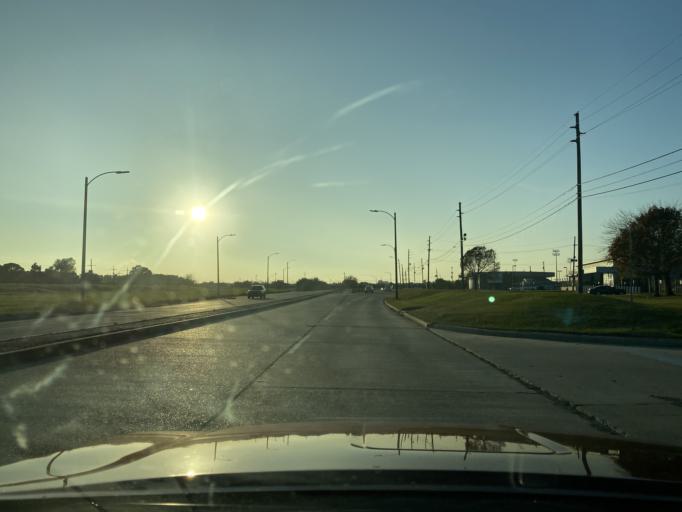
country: US
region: Louisiana
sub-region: Orleans Parish
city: New Orleans
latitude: 30.0300
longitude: -90.0420
